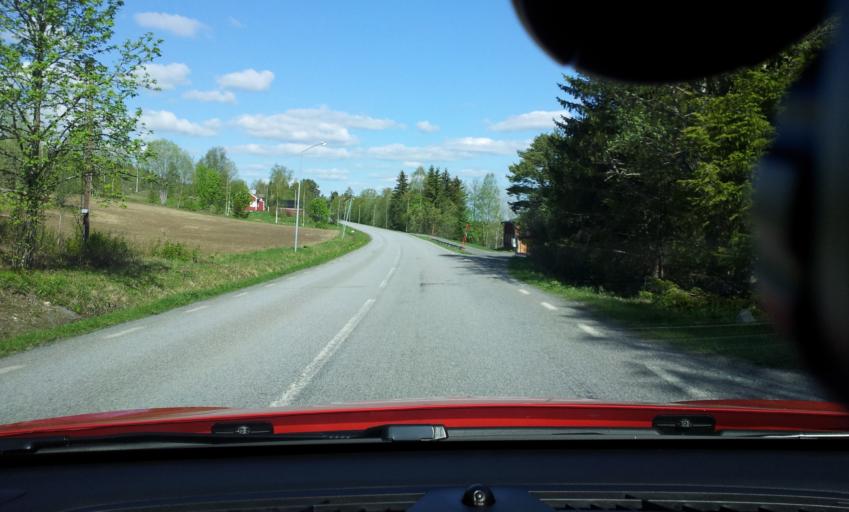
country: SE
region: Jaemtland
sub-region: Krokoms Kommun
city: Krokom
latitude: 63.1804
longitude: 14.0860
